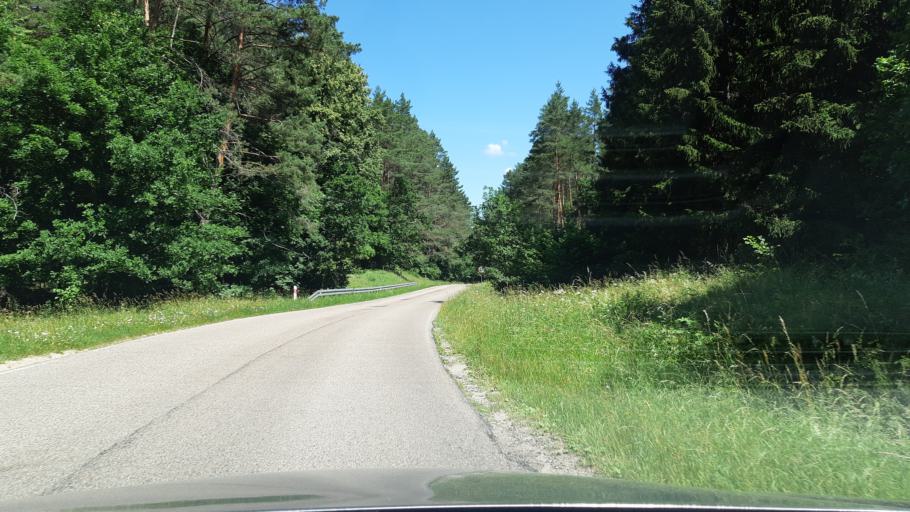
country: PL
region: Warmian-Masurian Voivodeship
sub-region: Powiat mragowski
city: Mikolajki
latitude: 53.7412
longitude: 21.5035
